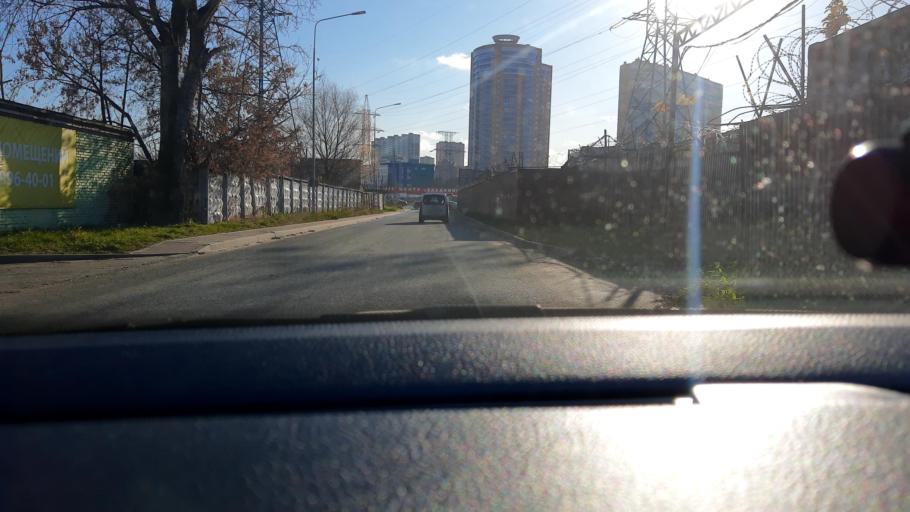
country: RU
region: Moscow
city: Ivanovskoye
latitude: 55.7797
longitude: 37.8471
